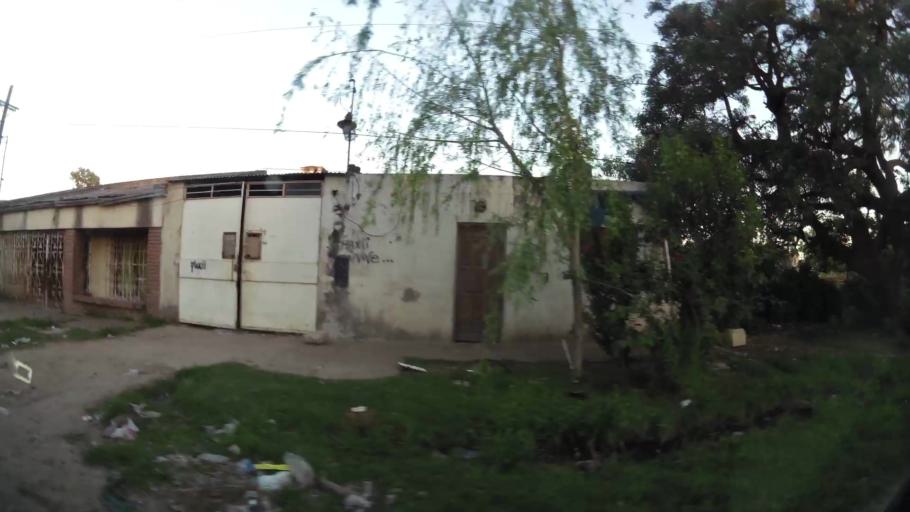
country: AR
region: Santa Fe
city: Santa Fe de la Vera Cruz
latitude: -31.5940
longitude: -60.6976
